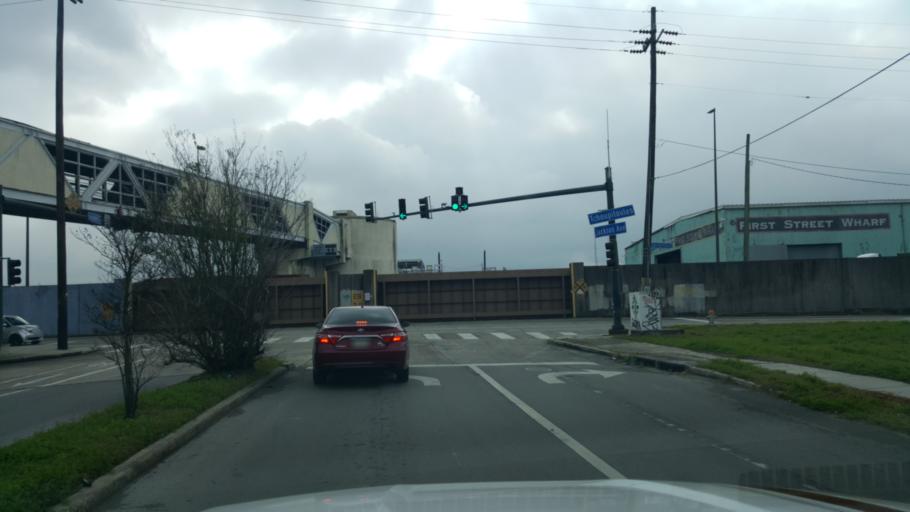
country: US
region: Louisiana
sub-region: Jefferson Parish
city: Gretna
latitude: 29.9236
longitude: -90.0716
